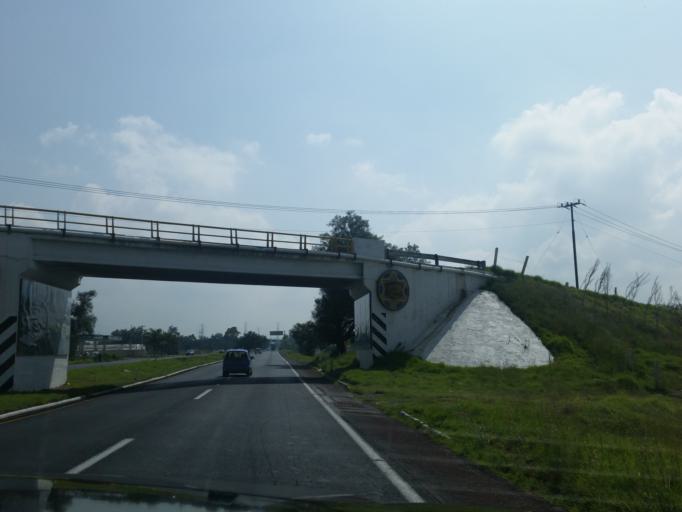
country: MX
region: Morelos
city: Xometla
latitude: 19.6479
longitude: -98.8886
